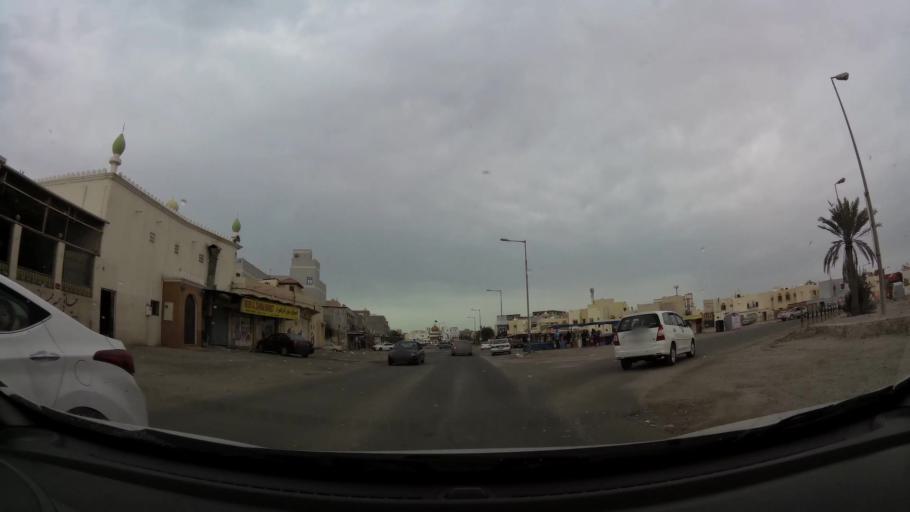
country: BH
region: Central Governorate
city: Madinat Hamad
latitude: 26.1251
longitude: 50.4775
